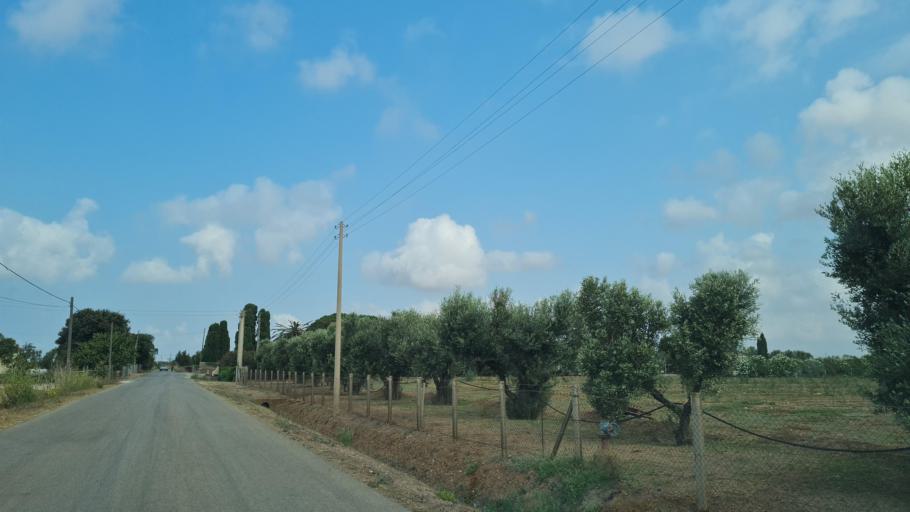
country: IT
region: Latium
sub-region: Provincia di Viterbo
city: Montalto di Castro
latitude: 42.3142
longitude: 11.6119
